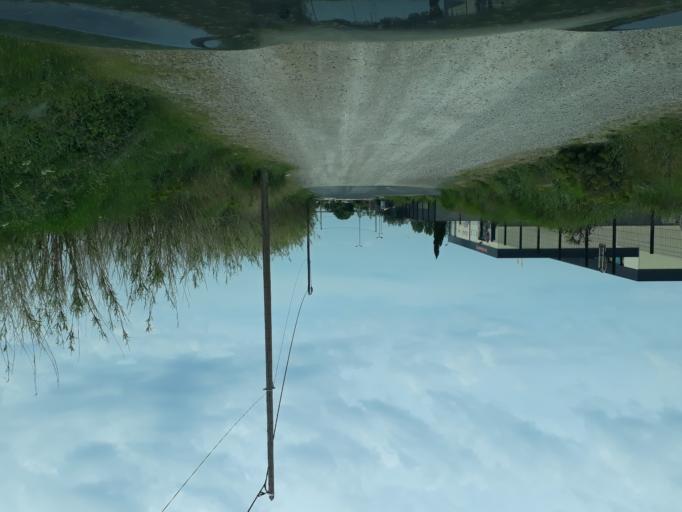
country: FR
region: Languedoc-Roussillon
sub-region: Departement de l'Herault
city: Agde
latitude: 43.2966
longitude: 3.4689
